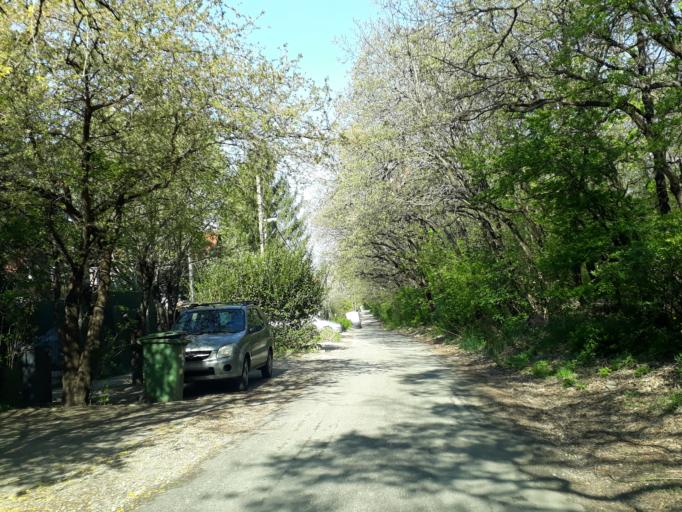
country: HU
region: Pest
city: Budakeszi
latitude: 47.5057
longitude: 18.9386
